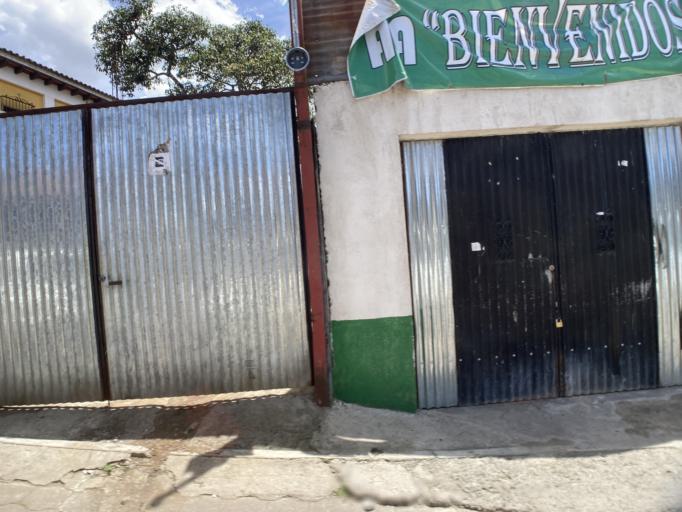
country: GT
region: Sacatepequez
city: Ciudad Vieja
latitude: 14.5242
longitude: -90.7499
